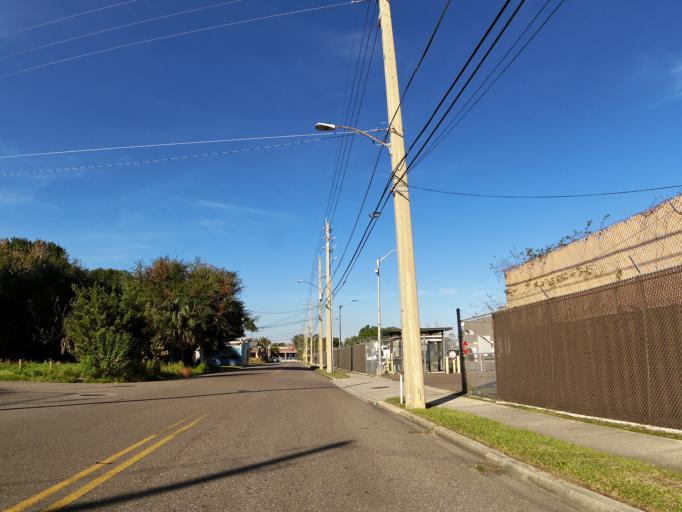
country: US
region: Florida
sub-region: Duval County
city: Jacksonville
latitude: 30.3372
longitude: -81.6730
